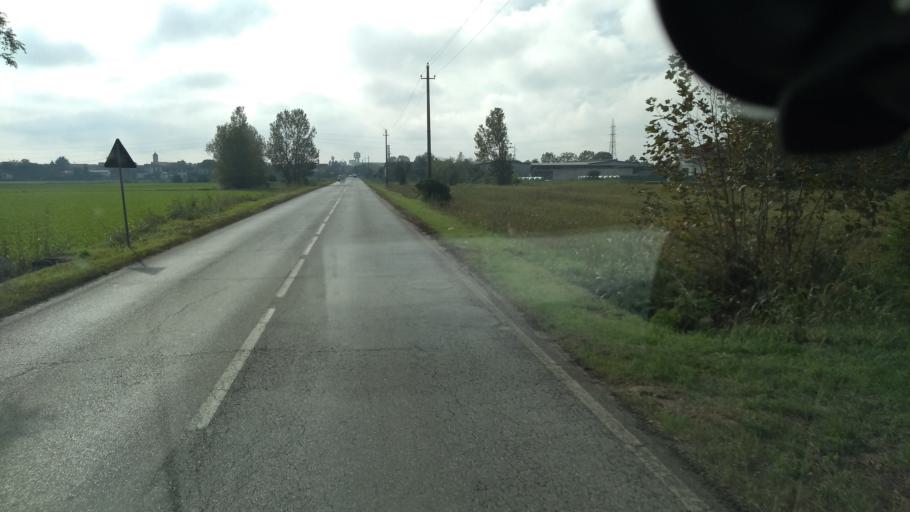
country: IT
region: Lombardy
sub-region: Provincia di Bergamo
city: Vidalengo
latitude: 45.5290
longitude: 9.6390
